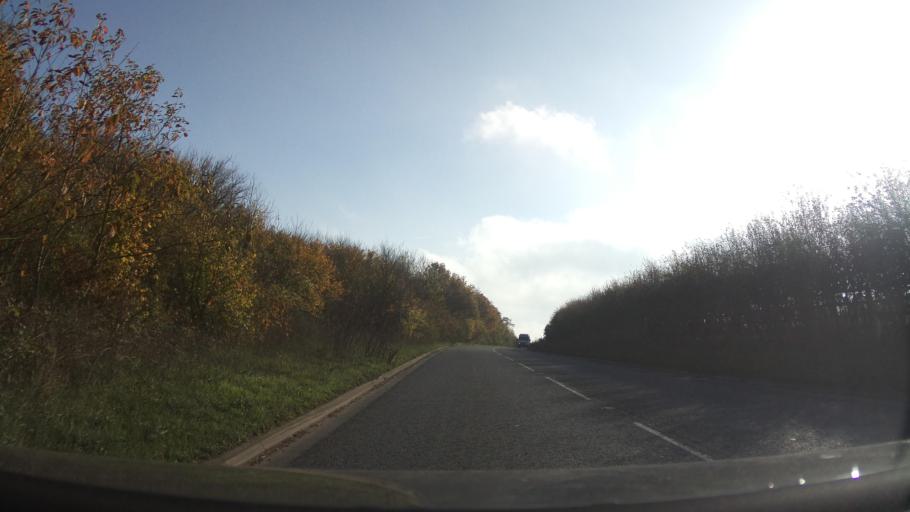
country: GB
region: England
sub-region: Wiltshire
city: Bradford-on-Avon
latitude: 51.3678
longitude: -2.2698
